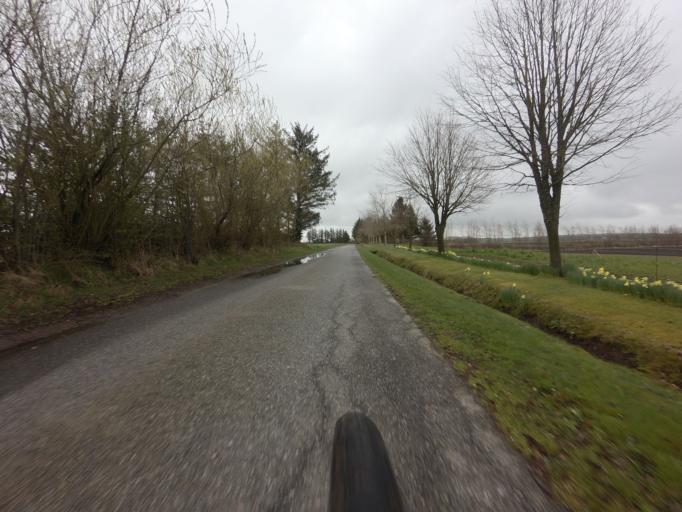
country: DK
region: North Denmark
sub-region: Jammerbugt Kommune
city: Pandrup
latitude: 57.3223
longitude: 9.7940
